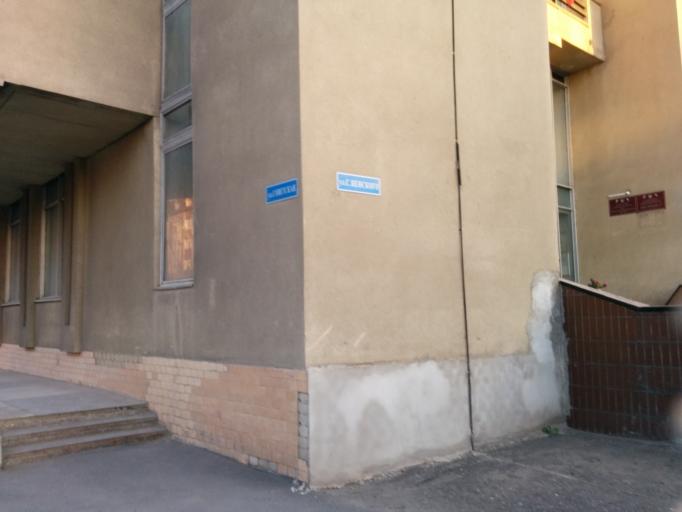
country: RU
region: Tambov
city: Tambov
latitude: 52.7098
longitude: 41.4653
